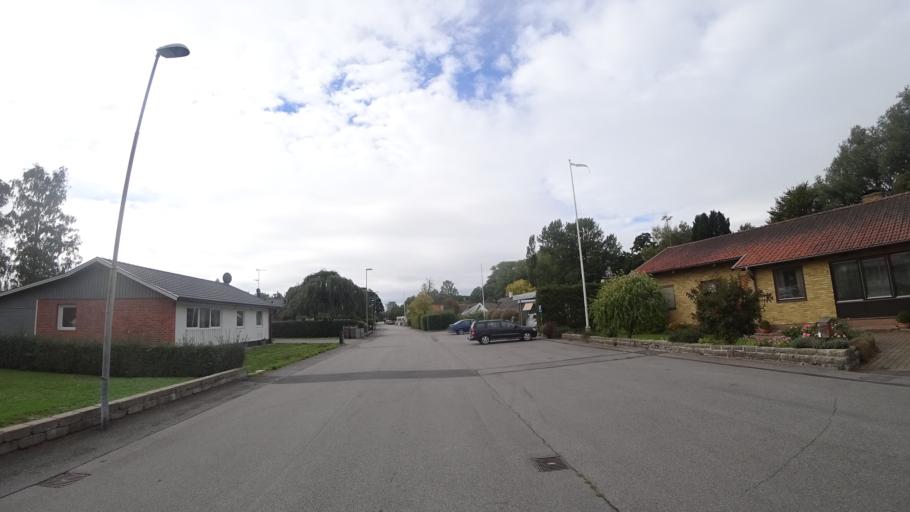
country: SE
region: Skane
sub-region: Kavlinge Kommun
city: Kaevlinge
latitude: 55.7808
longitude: 13.0849
